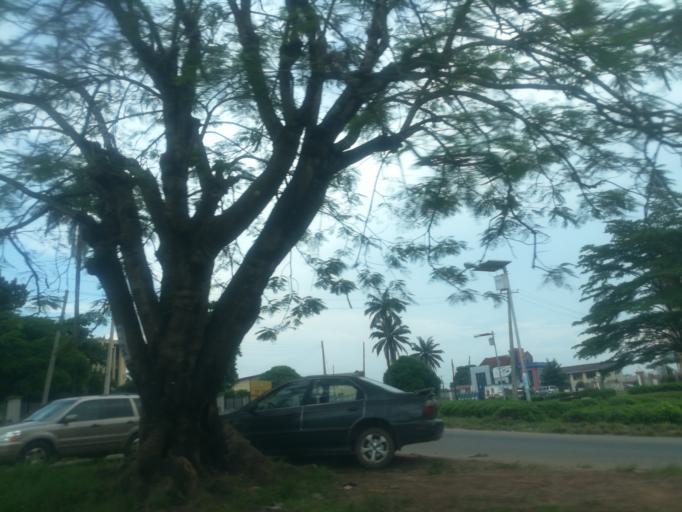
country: NG
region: Oyo
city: Ibadan
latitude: 7.4184
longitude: 3.9019
